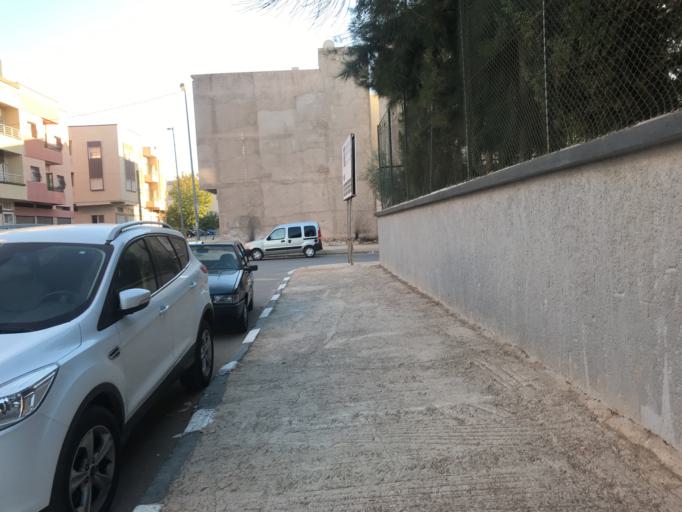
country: MA
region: Fes-Boulemane
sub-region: Fes
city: Fes
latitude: 34.0068
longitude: -5.0157
